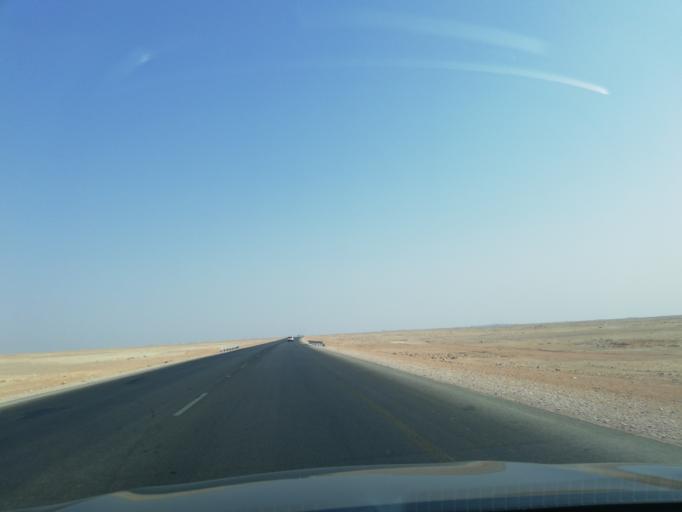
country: OM
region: Zufar
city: Salalah
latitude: 17.7662
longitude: 54.0167
